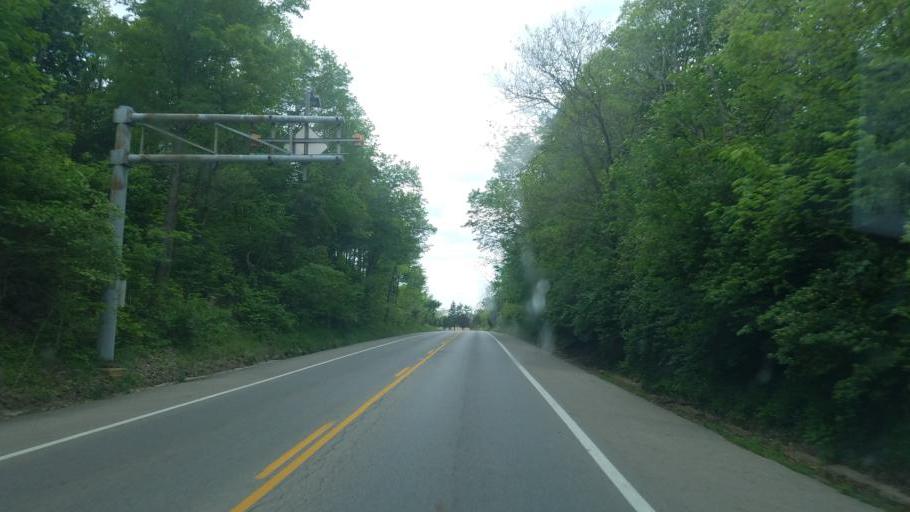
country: US
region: Ohio
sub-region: Franklin County
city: Grove City
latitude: 39.8058
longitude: -83.1745
